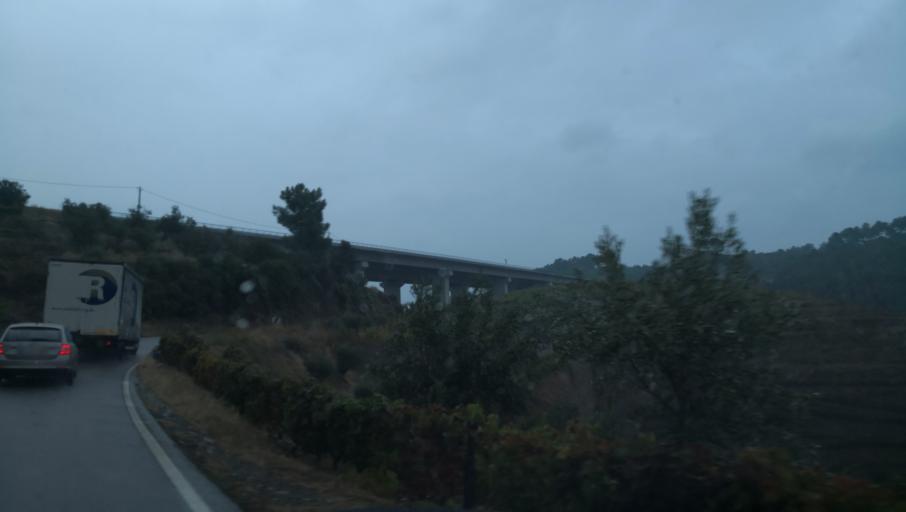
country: PT
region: Vila Real
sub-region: Vila Real
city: Vila Real
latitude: 41.2354
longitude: -7.7272
